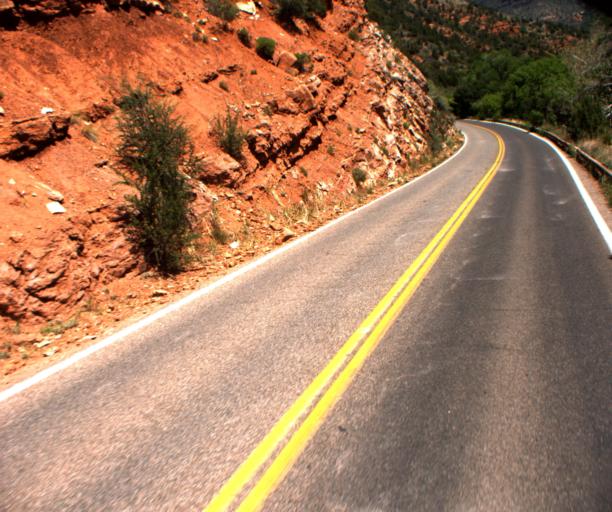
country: US
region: Arizona
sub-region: Coconino County
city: Sedona
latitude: 34.8965
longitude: -111.7322
